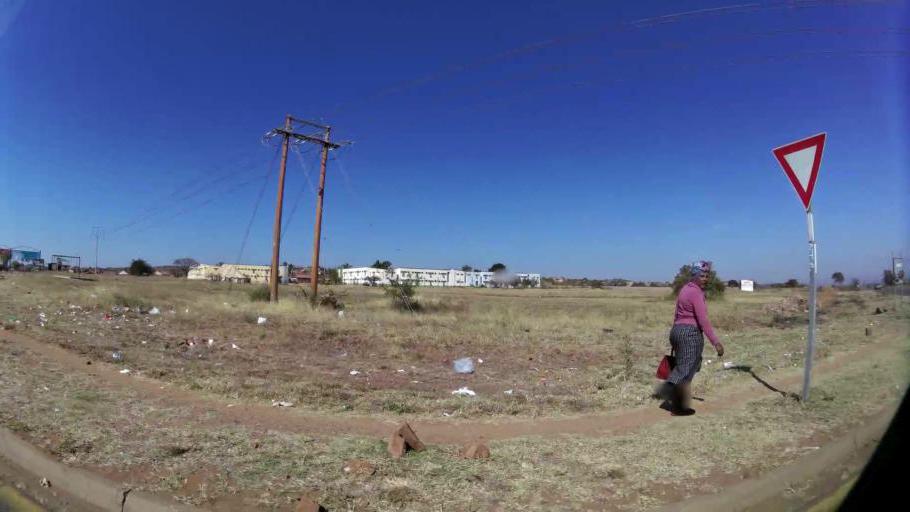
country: ZA
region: Gauteng
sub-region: City of Tshwane Metropolitan Municipality
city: Mabopane
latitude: -25.5213
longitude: 28.0892
